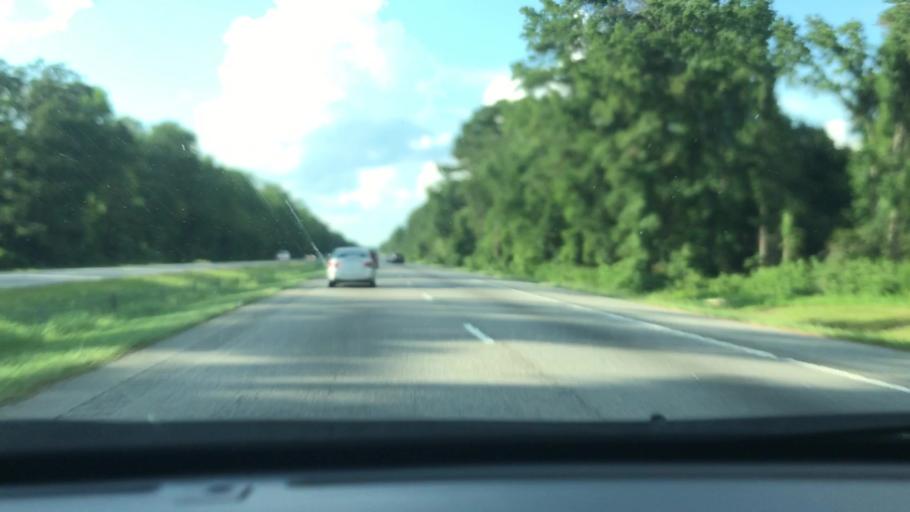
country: US
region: North Carolina
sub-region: Robeson County
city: Saint Pauls
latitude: 34.7348
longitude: -78.9972
